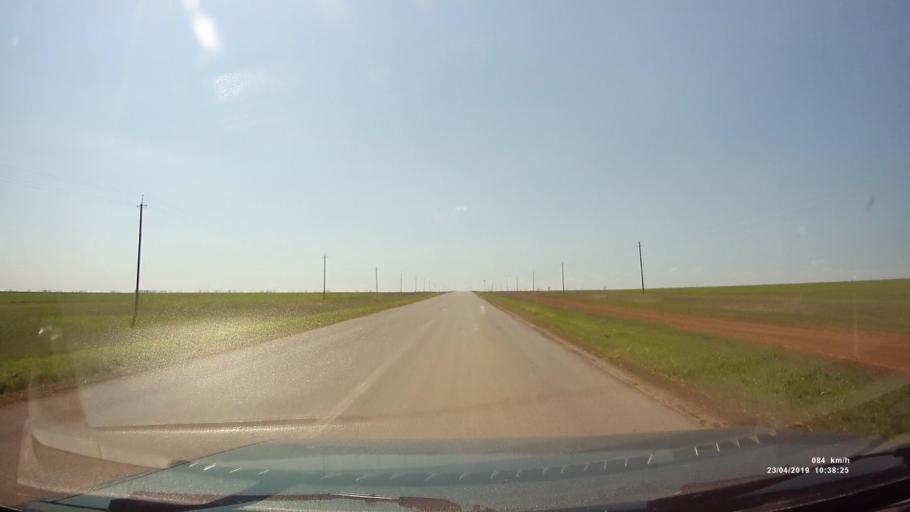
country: RU
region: Kalmykiya
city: Yashalta
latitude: 46.5328
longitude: 42.6388
